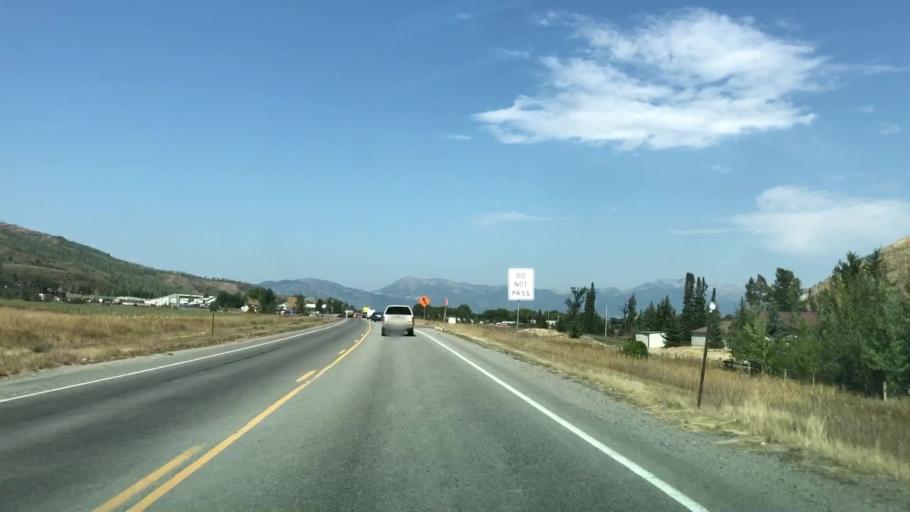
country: US
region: Wyoming
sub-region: Teton County
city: South Park
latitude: 43.3687
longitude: -110.7366
